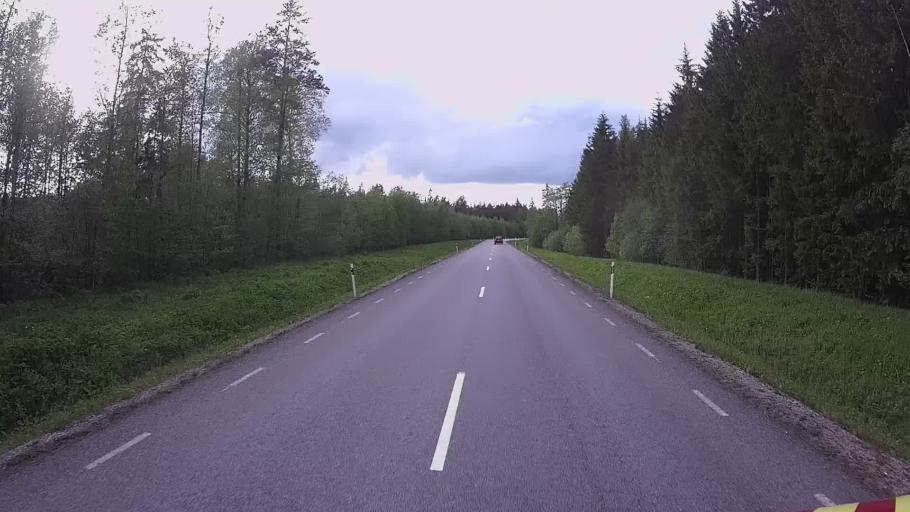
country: EE
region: Jogevamaa
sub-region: Mustvee linn
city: Mustvee
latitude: 59.0601
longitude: 27.0060
